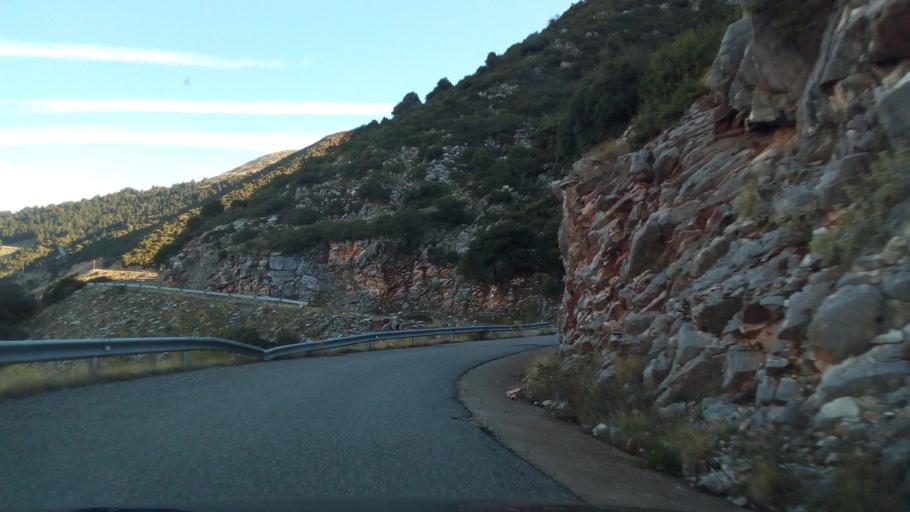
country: GR
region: West Greece
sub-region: Nomos Aitolias kai Akarnanias
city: Nafpaktos
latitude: 38.5143
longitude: 21.8466
